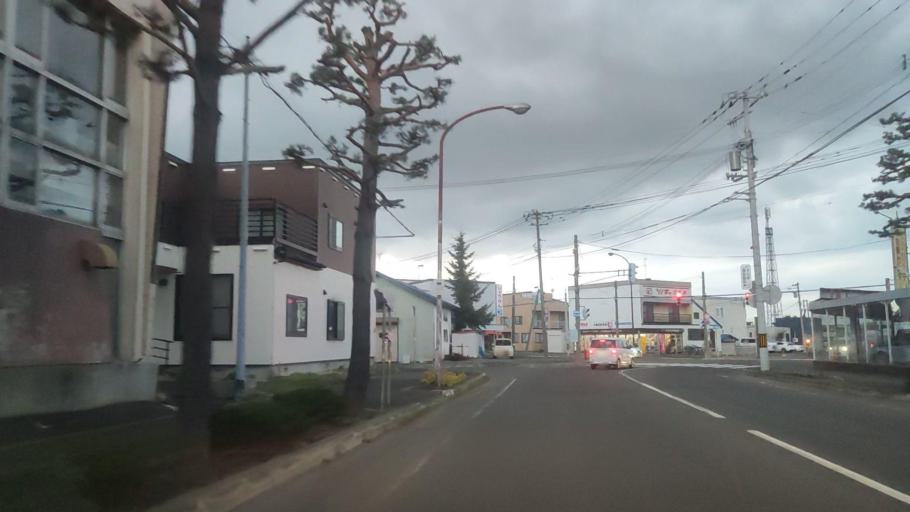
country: JP
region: Hokkaido
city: Shimo-furano
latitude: 43.3410
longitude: 142.3923
